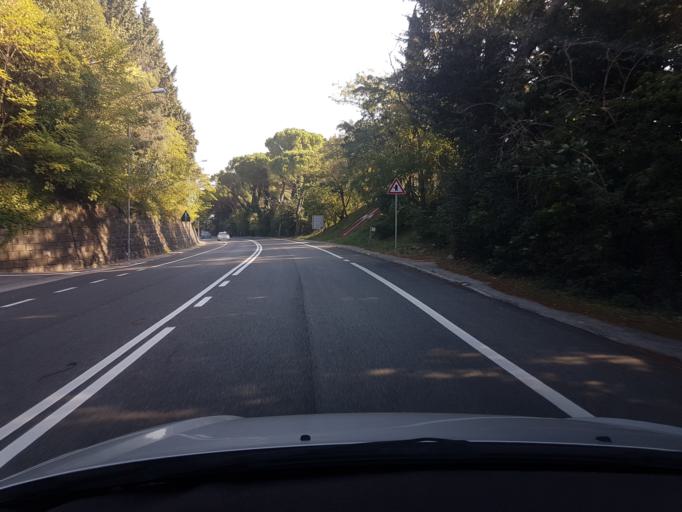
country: IT
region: Friuli Venezia Giulia
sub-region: Provincia di Trieste
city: Prosecco-Contovello
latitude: 45.7028
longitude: 13.7181
